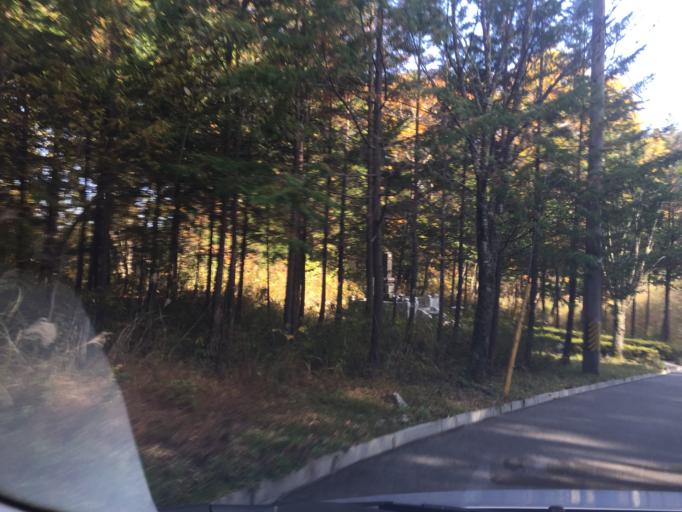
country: JP
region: Gifu
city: Nakatsugawa
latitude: 35.3691
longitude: 137.6708
